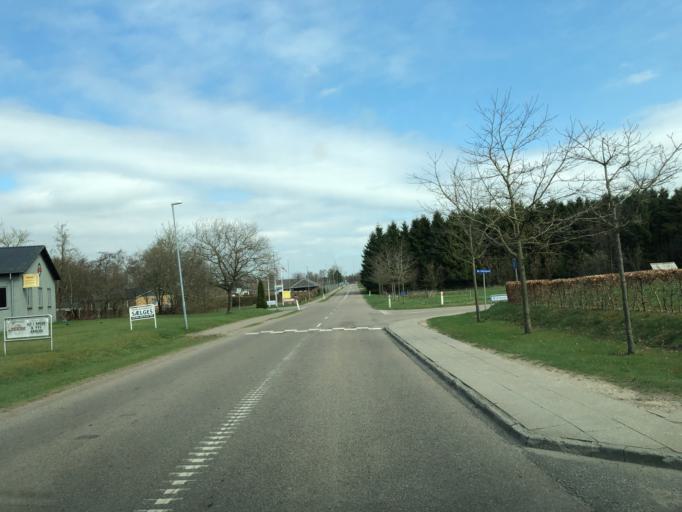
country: DK
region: South Denmark
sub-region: Vejle Kommune
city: Give
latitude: 55.9028
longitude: 9.2632
